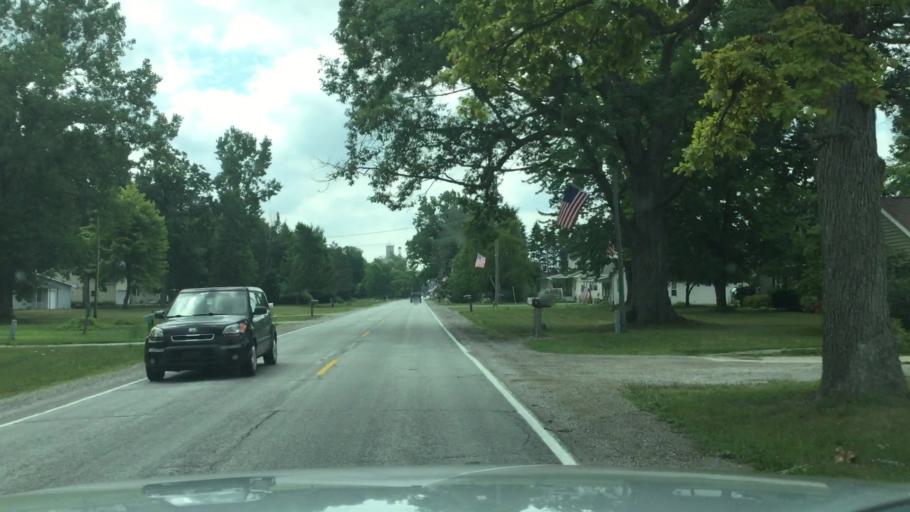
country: US
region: Michigan
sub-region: Saginaw County
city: Birch Run
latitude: 43.2581
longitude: -83.7944
